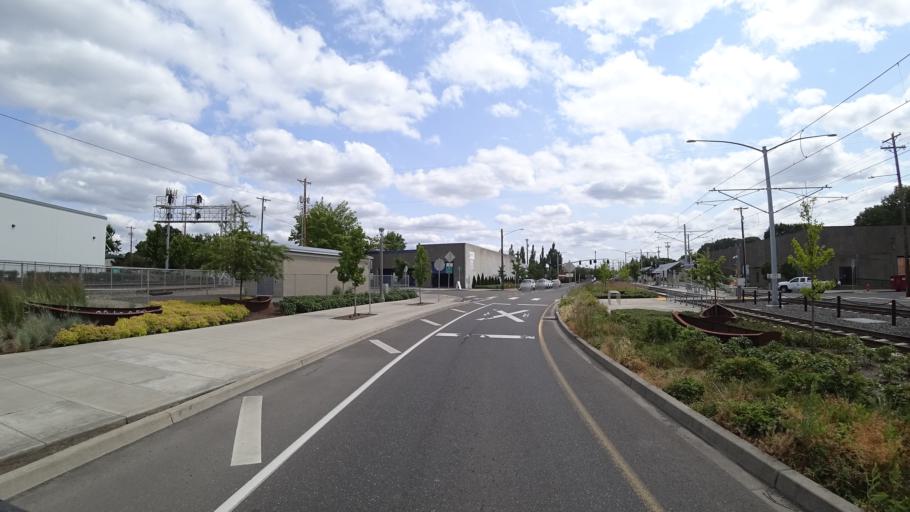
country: US
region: Oregon
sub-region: Multnomah County
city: Portland
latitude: 45.4985
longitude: -122.6480
